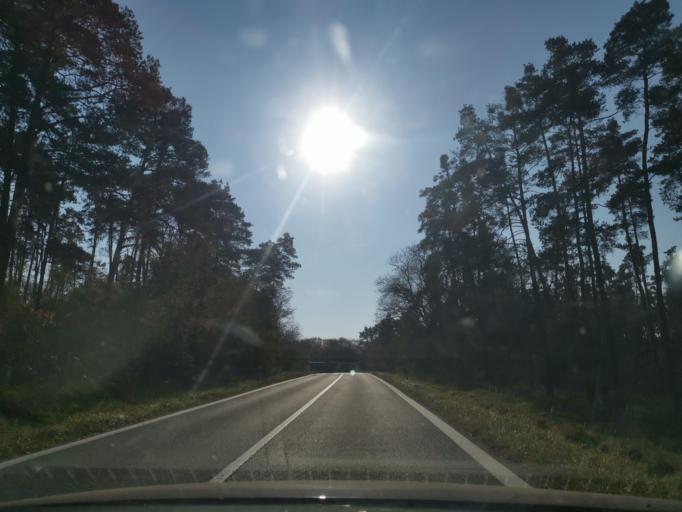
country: SK
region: Bratislavsky
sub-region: Okres Malacky
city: Malacky
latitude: 48.5144
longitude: 17.1252
